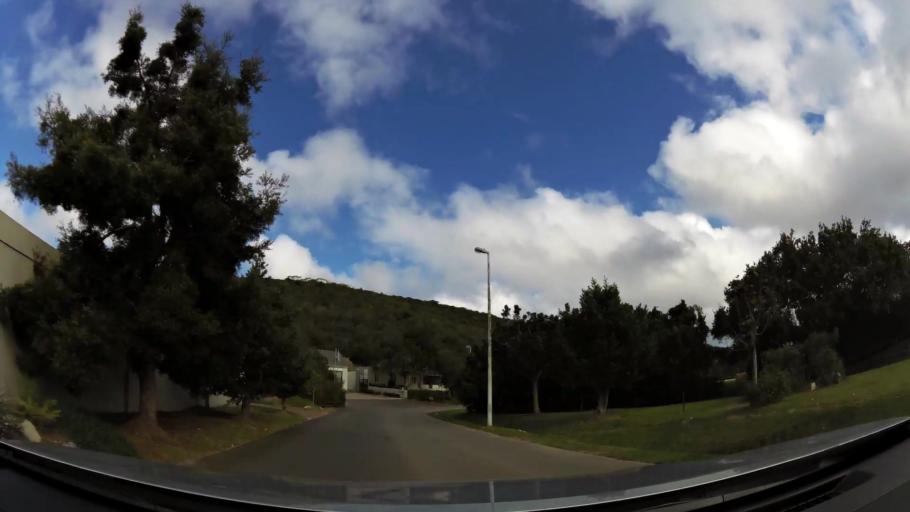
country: ZA
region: Western Cape
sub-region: Eden District Municipality
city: Plettenberg Bay
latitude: -34.0624
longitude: 23.3569
